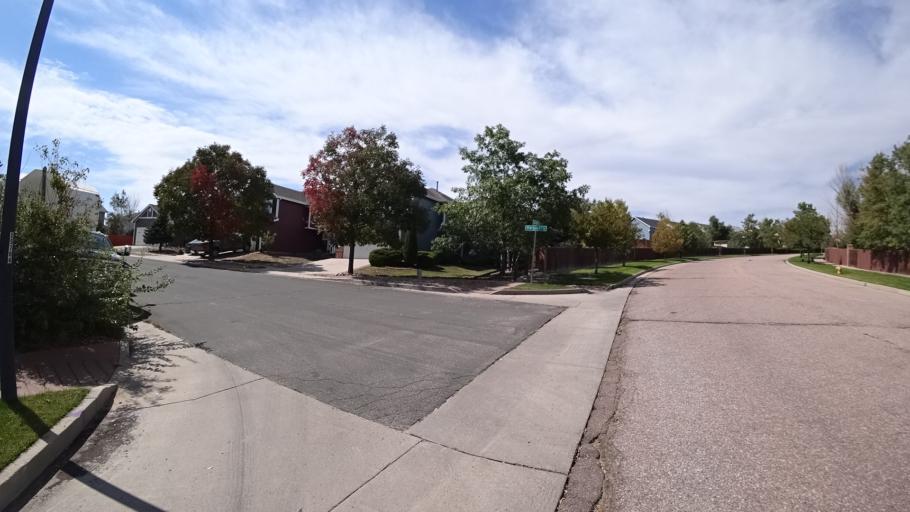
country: US
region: Colorado
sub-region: El Paso County
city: Cimarron Hills
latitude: 38.8994
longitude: -104.7127
